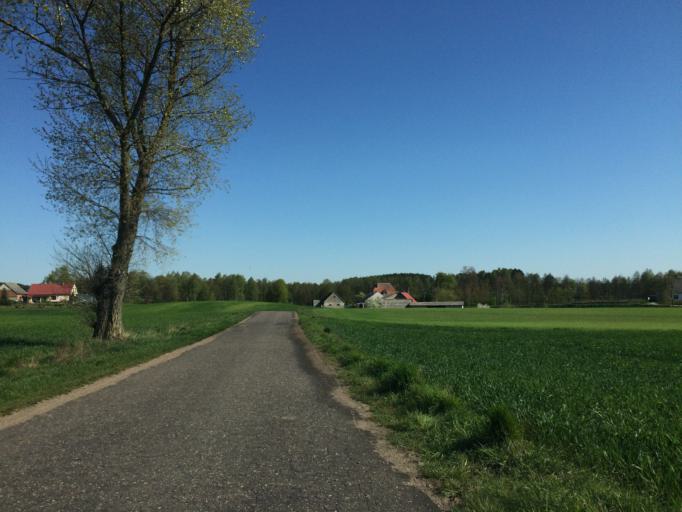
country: PL
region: Warmian-Masurian Voivodeship
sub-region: Powiat dzialdowski
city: Rybno
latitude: 53.4411
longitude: 19.9208
